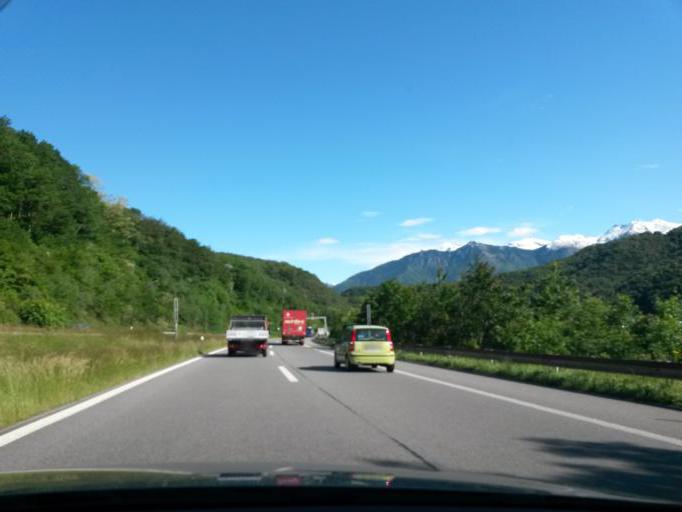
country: CH
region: Ticino
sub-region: Bellinzona District
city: Cadenazzo
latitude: 46.1237
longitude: 8.9201
